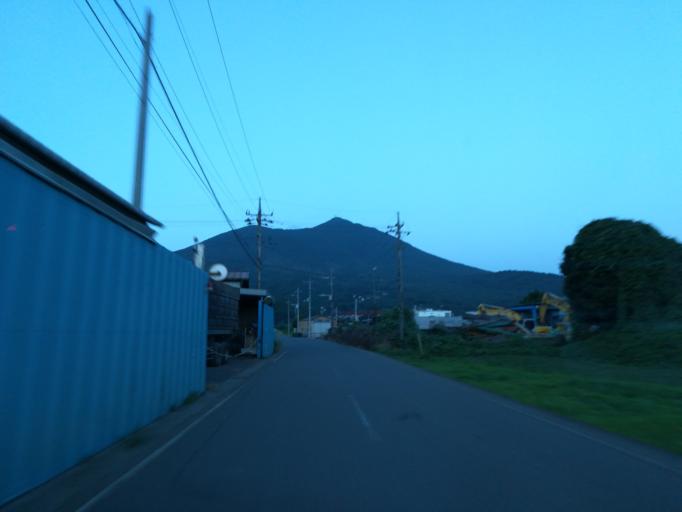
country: JP
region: Ibaraki
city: Makabe
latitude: 36.2364
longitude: 140.0563
